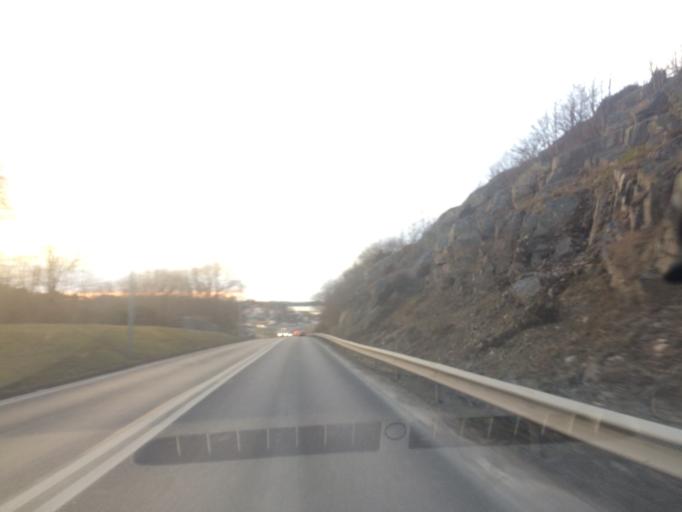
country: SE
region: Vaestra Goetaland
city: Hjuvik
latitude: 57.7110
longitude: 11.7306
